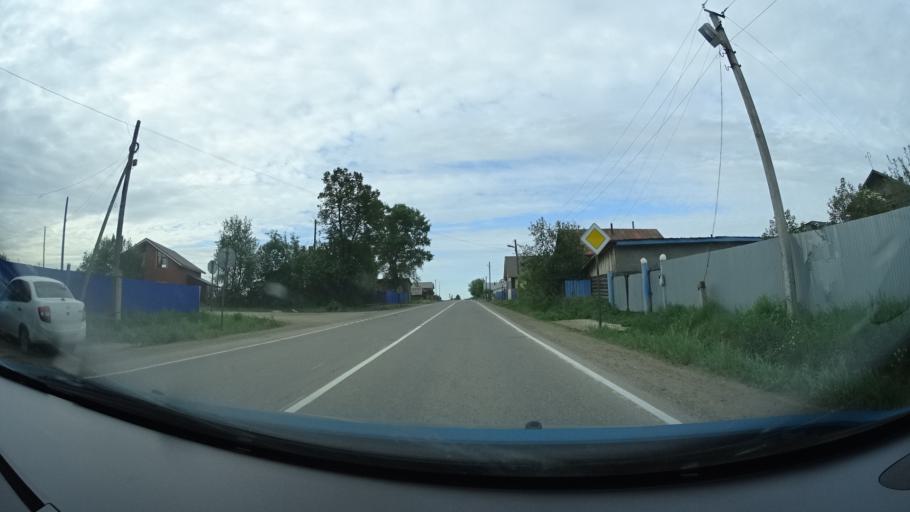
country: RU
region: Perm
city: Barda
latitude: 56.8827
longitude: 55.6007
